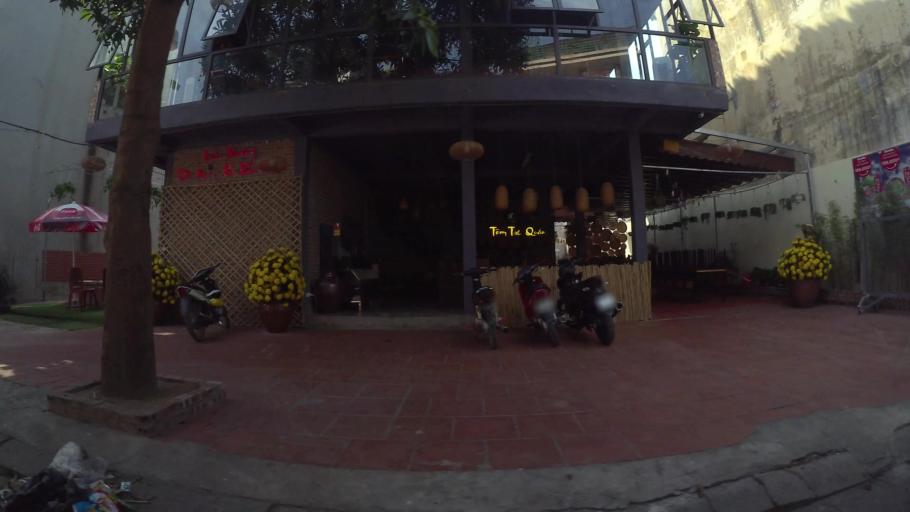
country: VN
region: Ha Noi
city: Hoan Kiem
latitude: 21.0497
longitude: 105.8661
